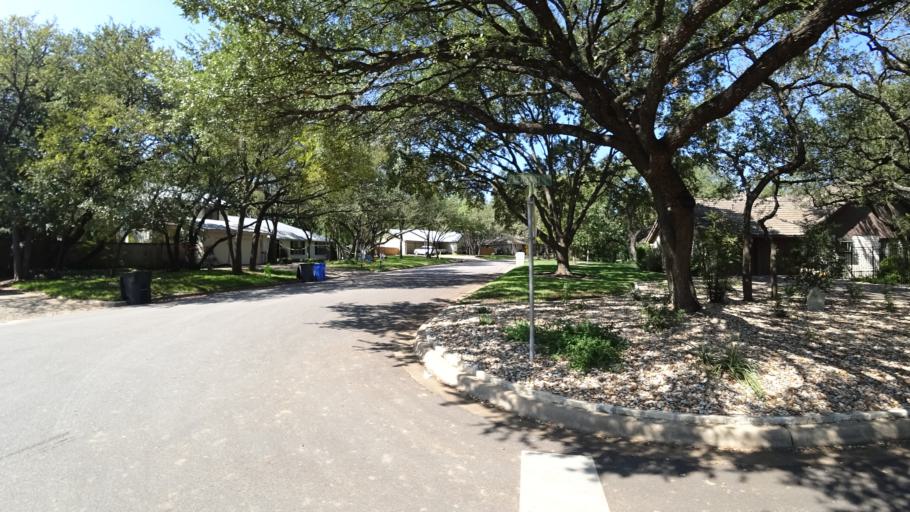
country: US
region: Texas
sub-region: Travis County
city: Rollingwood
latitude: 30.2772
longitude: -97.7887
